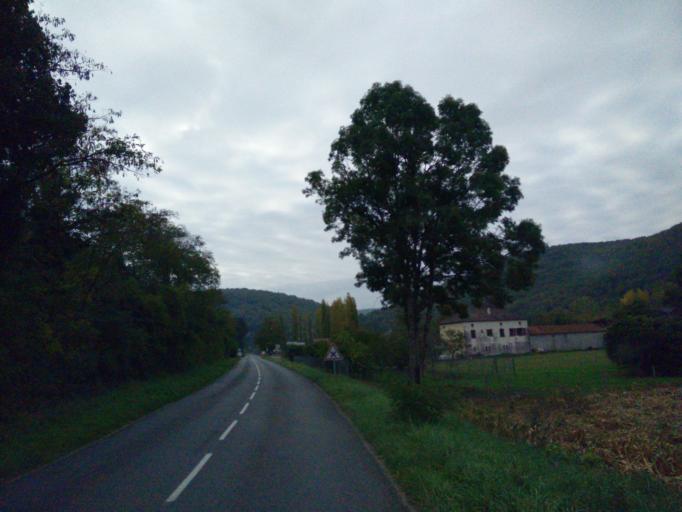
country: FR
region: Midi-Pyrenees
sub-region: Departement du Lot
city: Lalbenque
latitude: 44.4723
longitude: 1.5870
